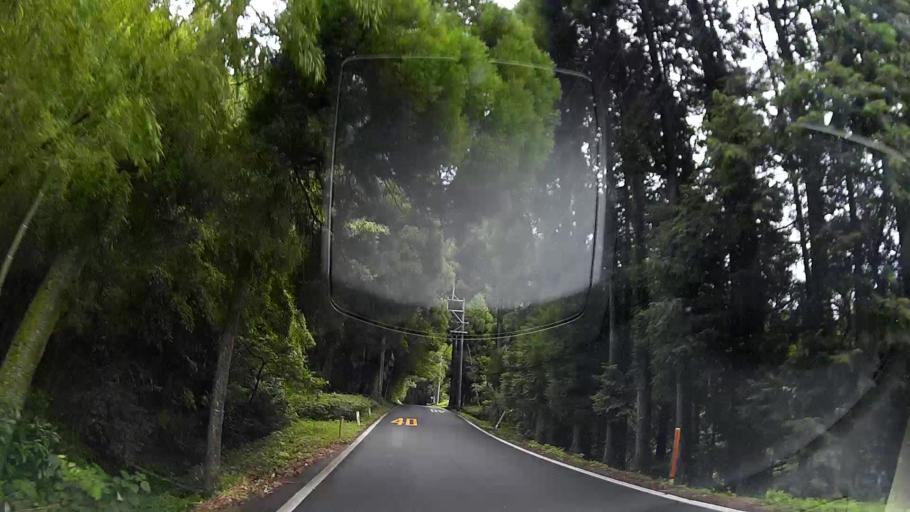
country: JP
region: Kumamoto
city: Kikuchi
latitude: 33.0988
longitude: 130.9604
